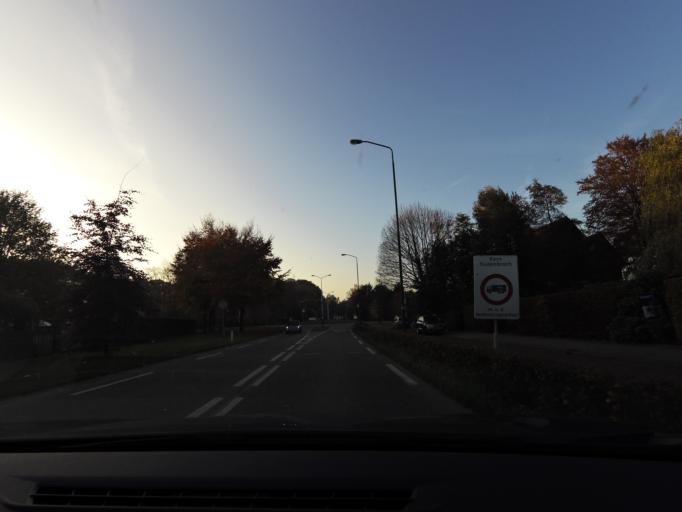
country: NL
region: North Brabant
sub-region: Gemeente Rucphen
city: Rucphen
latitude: 51.5837
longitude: 4.5849
